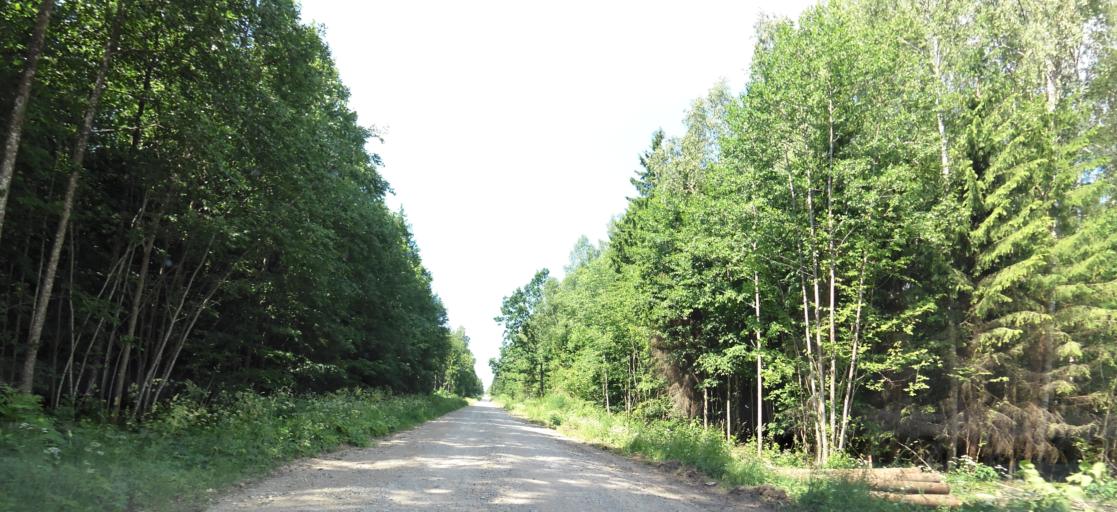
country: LT
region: Panevezys
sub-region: Birzai
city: Birzai
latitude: 56.2298
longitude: 24.9714
